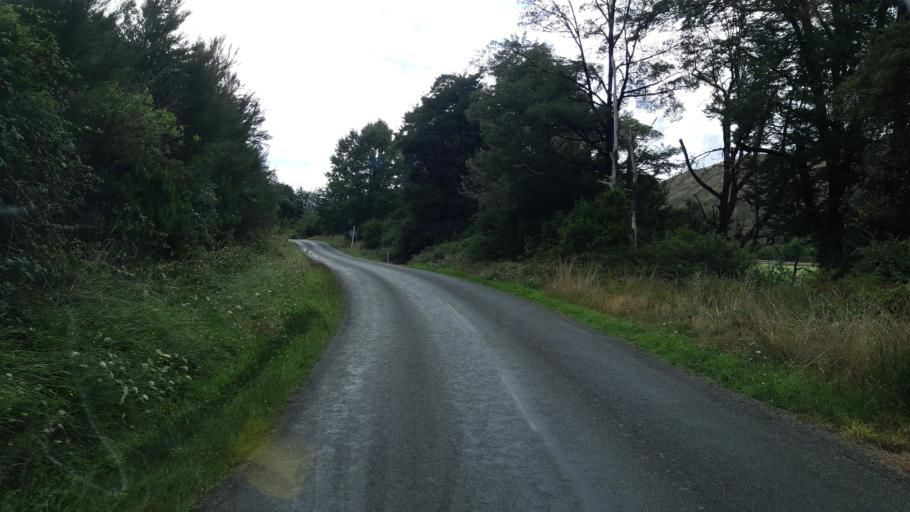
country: NZ
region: West Coast
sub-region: Buller District
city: Westport
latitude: -41.7890
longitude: 172.3653
